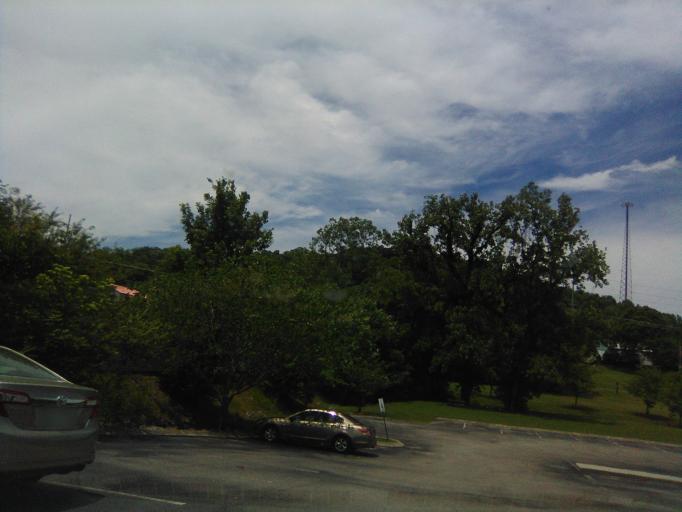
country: US
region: Tennessee
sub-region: Davidson County
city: Belle Meade
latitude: 36.1249
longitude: -86.9084
